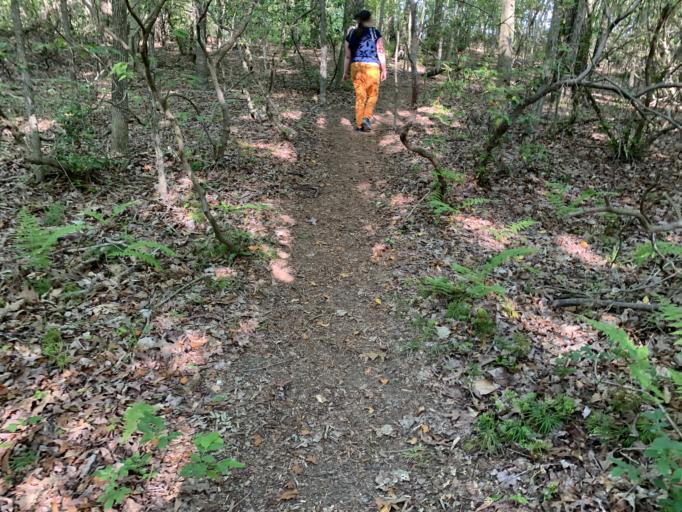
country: US
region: Maryland
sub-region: Cecil County
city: North East
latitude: 39.5748
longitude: -75.8857
